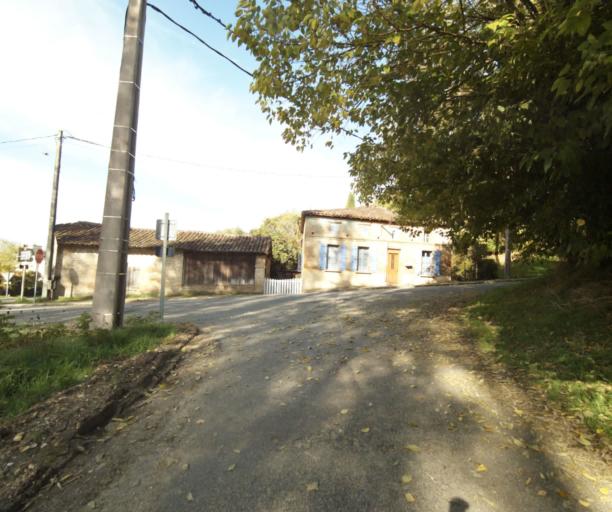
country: FR
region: Midi-Pyrenees
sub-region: Departement du Tarn-et-Garonne
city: Nohic
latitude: 43.9050
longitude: 1.4542
